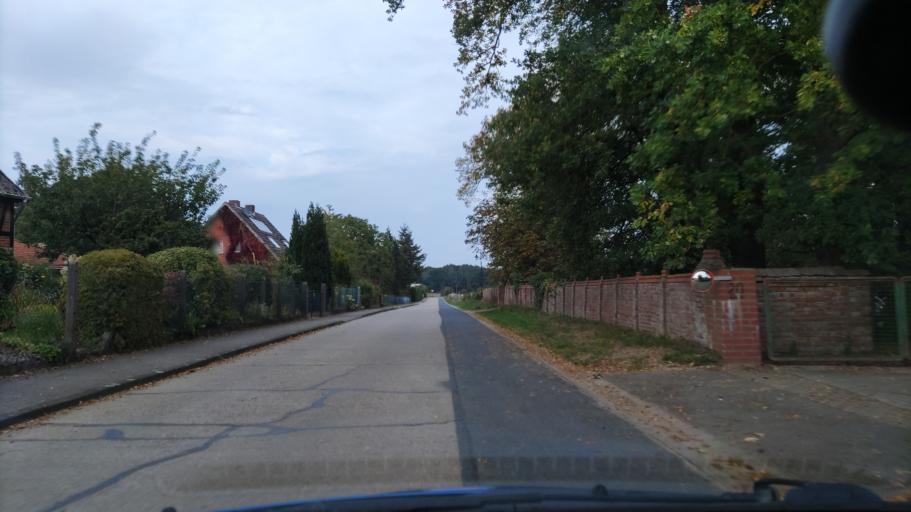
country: DE
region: Lower Saxony
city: Karwitz
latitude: 53.0903
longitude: 11.0115
